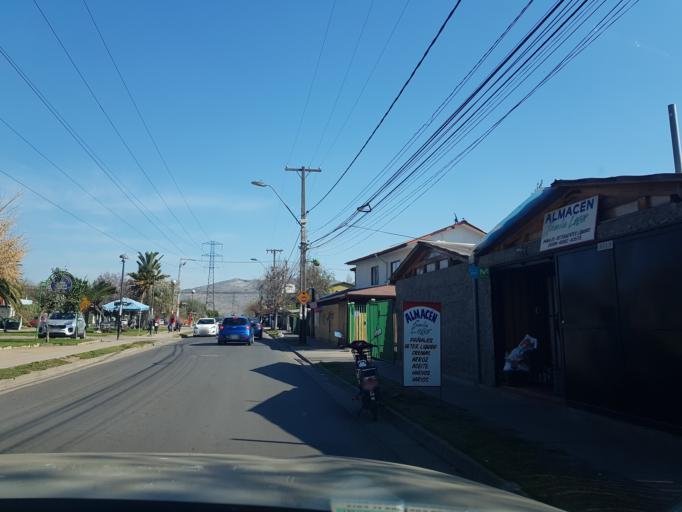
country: CL
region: Santiago Metropolitan
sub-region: Provincia de Santiago
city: Lo Prado
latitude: -33.3695
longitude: -70.7209
